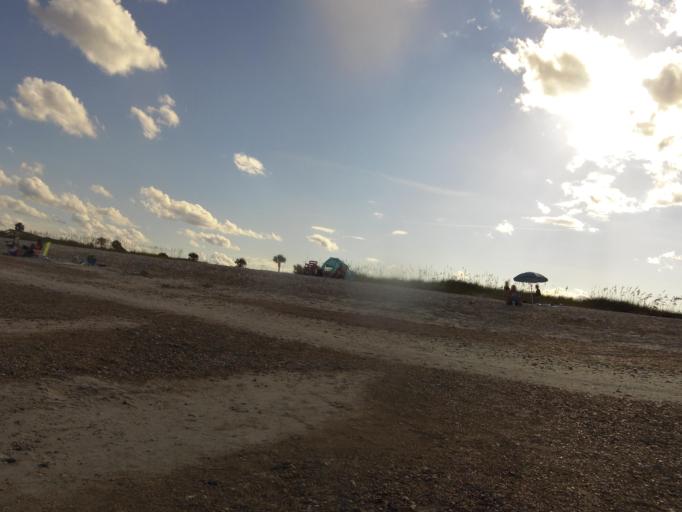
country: US
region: Florida
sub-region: Nassau County
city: Fernandina Beach
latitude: 30.6705
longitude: -81.4297
